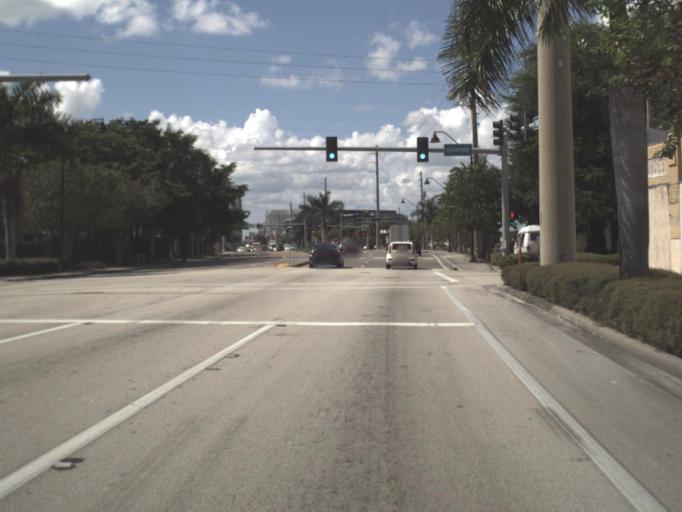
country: US
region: Florida
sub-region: Lee County
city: Fort Myers
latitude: 26.6409
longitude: -81.8579
